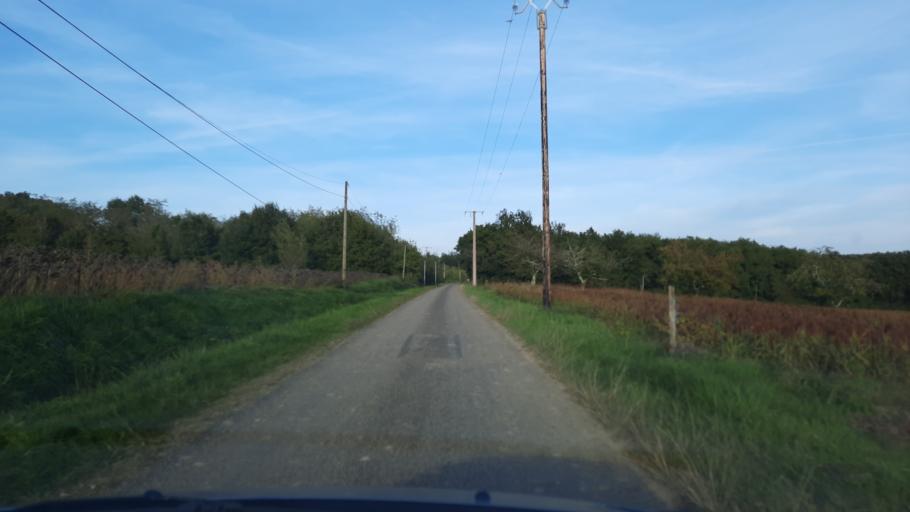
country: FR
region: Midi-Pyrenees
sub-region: Departement du Tarn-et-Garonne
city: Molieres
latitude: 44.1745
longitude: 1.3015
